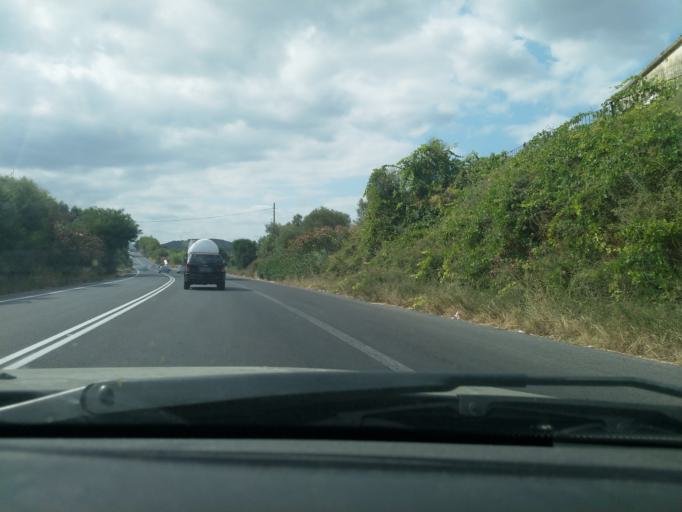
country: GR
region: Crete
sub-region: Nomos Chanias
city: Georgioupolis
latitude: 35.3611
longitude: 24.2489
